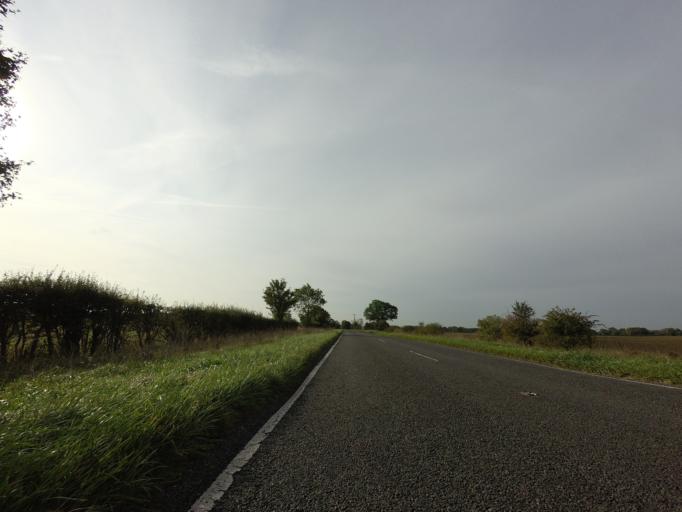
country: GB
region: England
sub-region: Cambridgeshire
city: Harston
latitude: 52.1028
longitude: 0.0842
